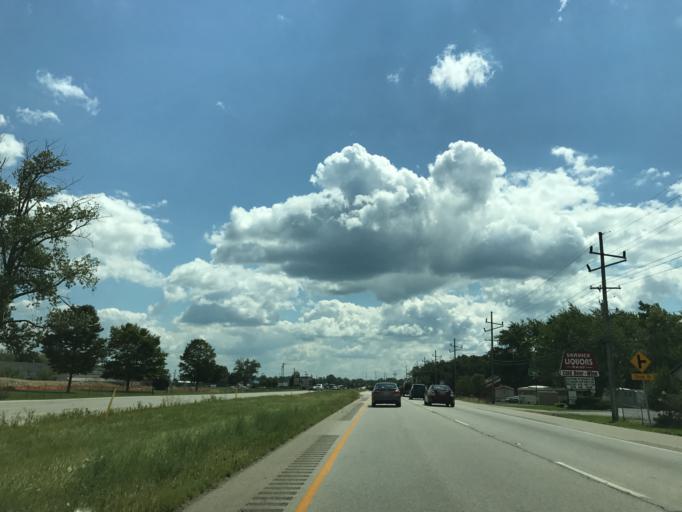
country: US
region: Indiana
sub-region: Kosciusko County
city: Winona Lake
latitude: 41.2298
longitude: -85.7994
